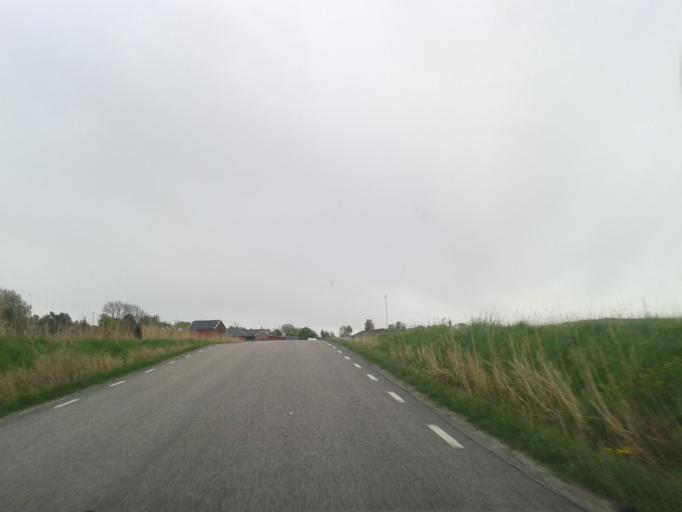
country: SE
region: Vaestra Goetaland
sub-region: Kungalvs Kommun
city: Kode
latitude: 57.9496
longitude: 11.8187
